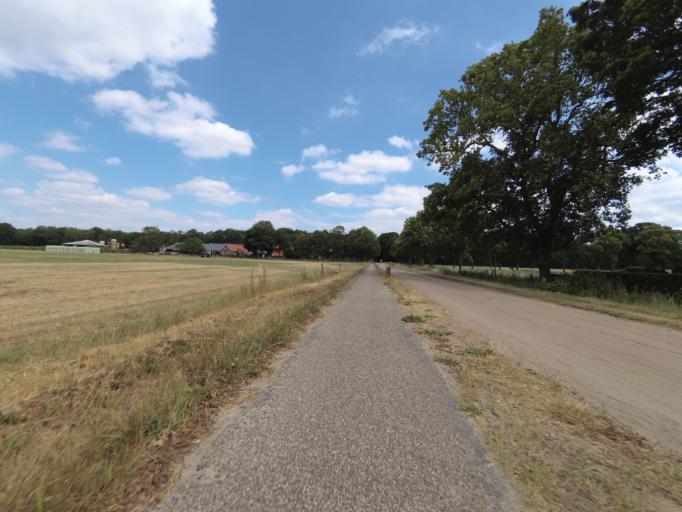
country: NL
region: Overijssel
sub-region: Gemeente Wierden
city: Wierden
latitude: 52.3494
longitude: 6.5067
